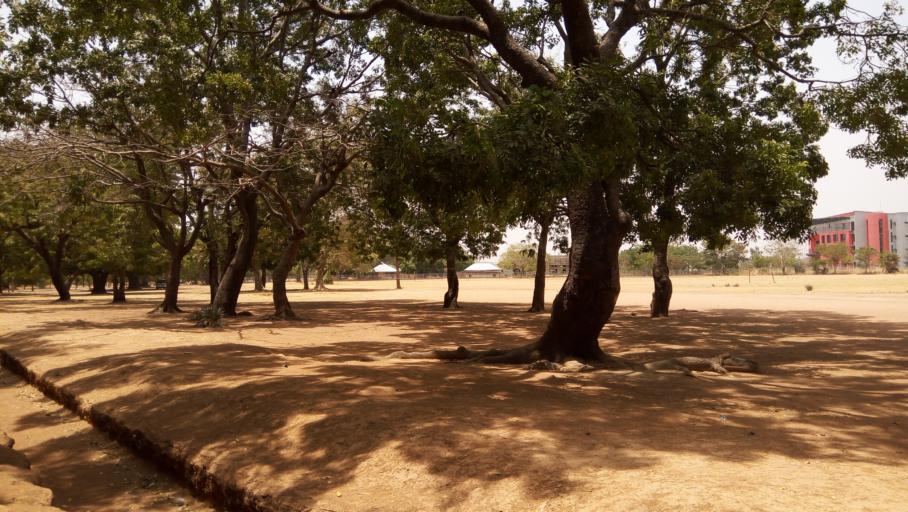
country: NG
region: Kaduna
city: Zaria
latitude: 11.1460
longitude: 7.6541
